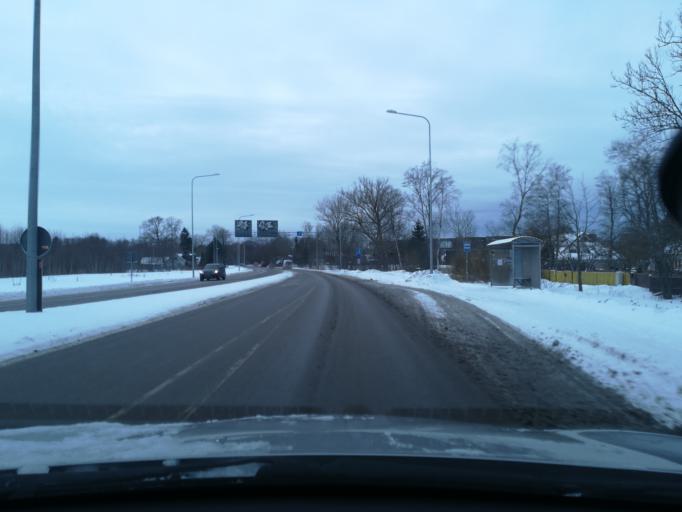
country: EE
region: Harju
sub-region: Harku vald
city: Tabasalu
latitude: 59.4371
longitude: 24.5721
